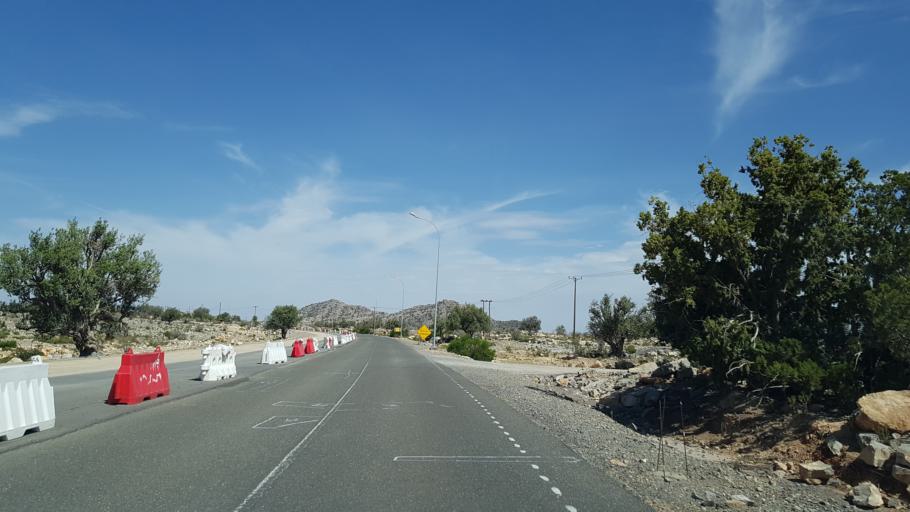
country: OM
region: Muhafazat ad Dakhiliyah
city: Nizwa
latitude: 23.1188
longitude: 57.6245
